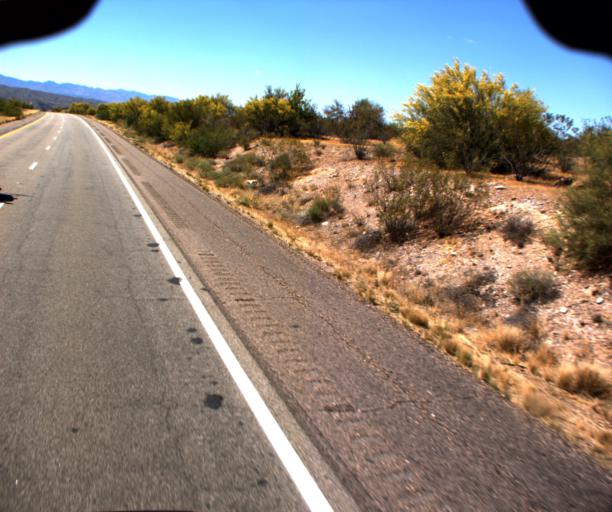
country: US
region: Arizona
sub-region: Yavapai County
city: Bagdad
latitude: 34.6270
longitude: -113.5378
